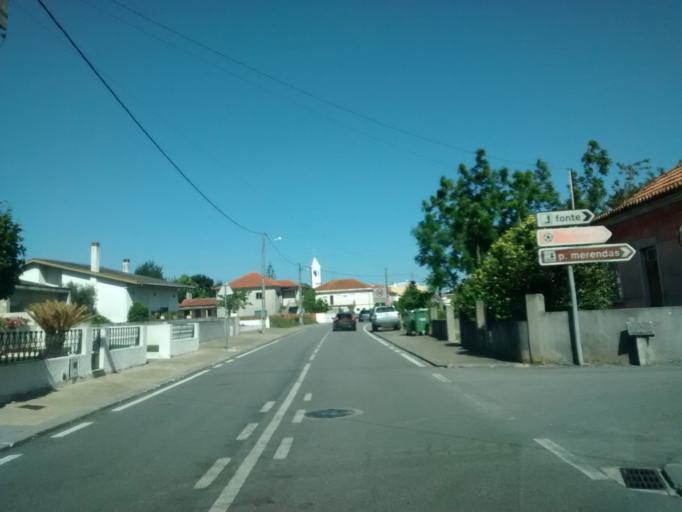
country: PT
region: Coimbra
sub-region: Mira
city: Mira
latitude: 40.4273
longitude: -8.6786
